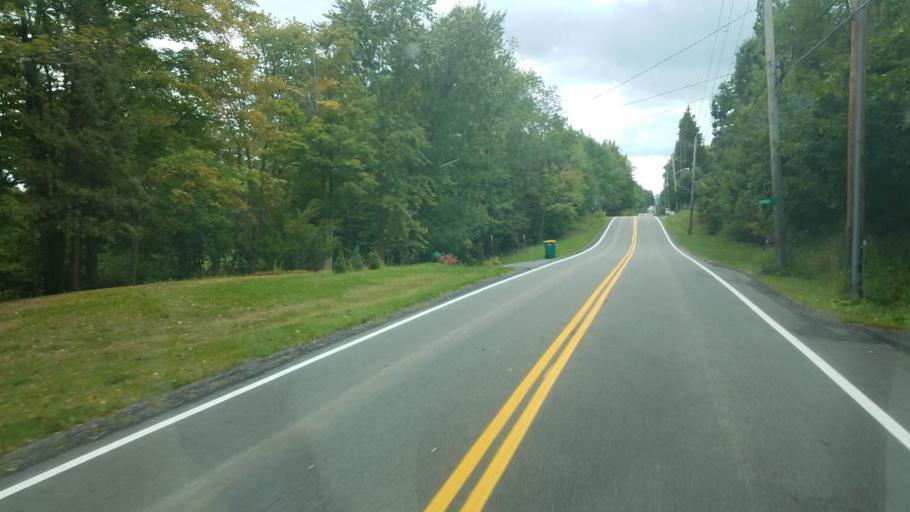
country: US
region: Ohio
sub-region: Geauga County
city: Burton
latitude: 41.5180
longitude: -81.1804
